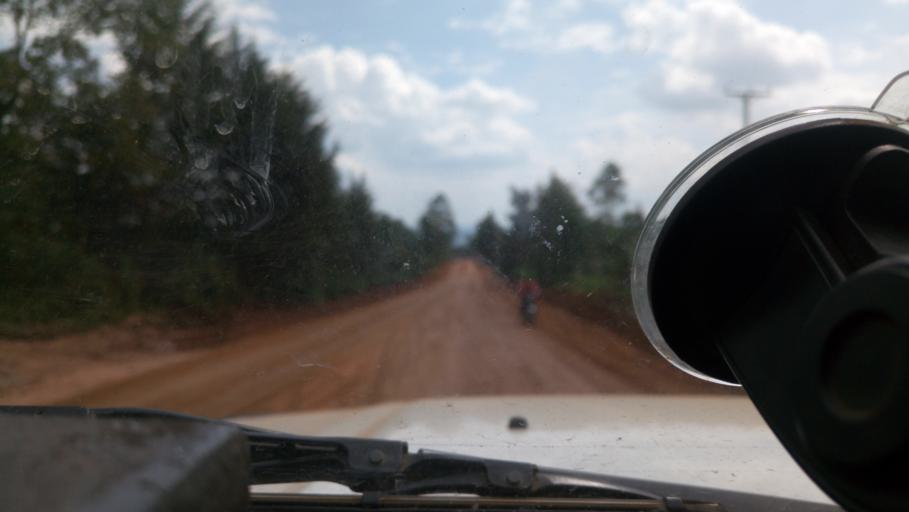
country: KE
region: Kericho
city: Litein
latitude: -0.5821
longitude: 35.1260
